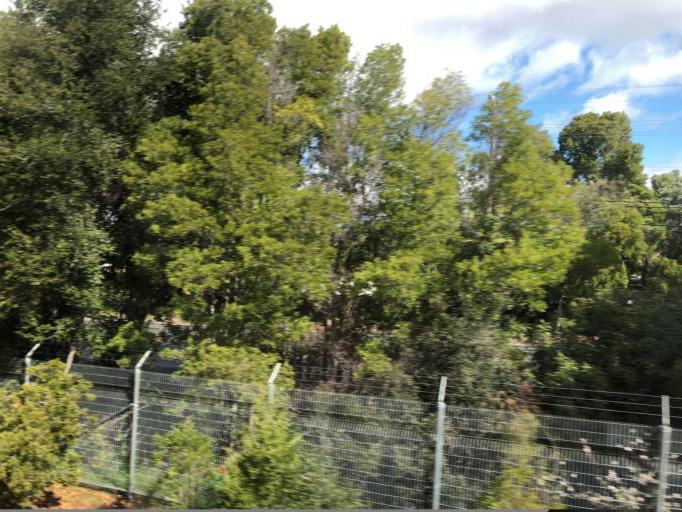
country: US
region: California
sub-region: Santa Clara County
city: Los Altos
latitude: 37.4156
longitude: -122.1202
